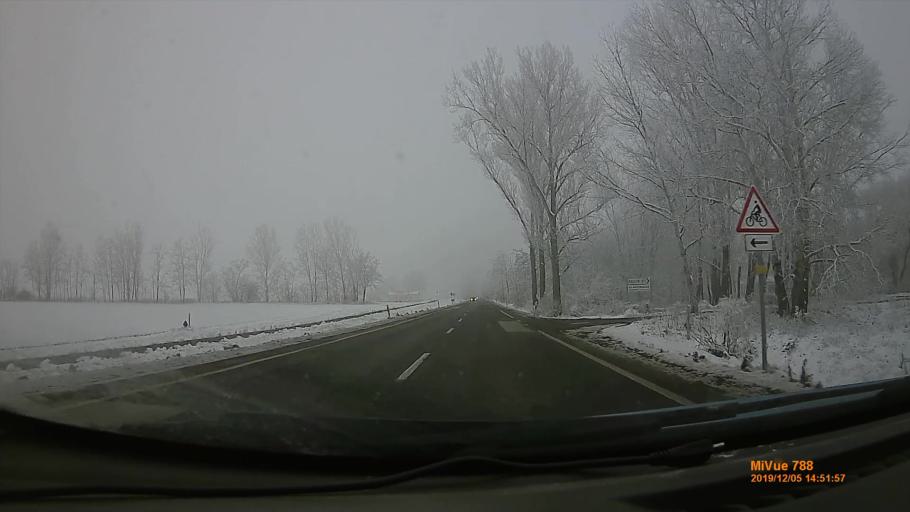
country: HU
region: Szabolcs-Szatmar-Bereg
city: Nyirtelek
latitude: 47.9970
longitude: 21.6505
